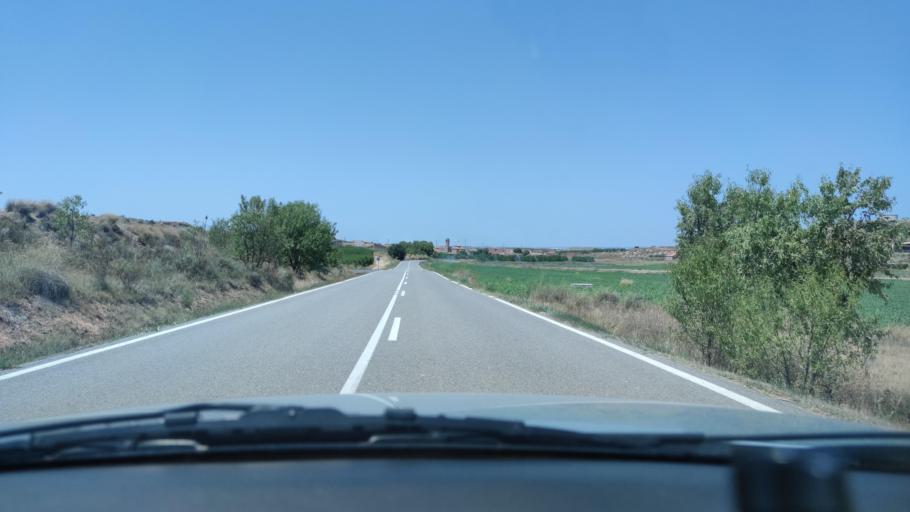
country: ES
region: Catalonia
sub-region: Provincia de Lleida
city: Alcano
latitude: 41.4754
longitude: 0.6235
